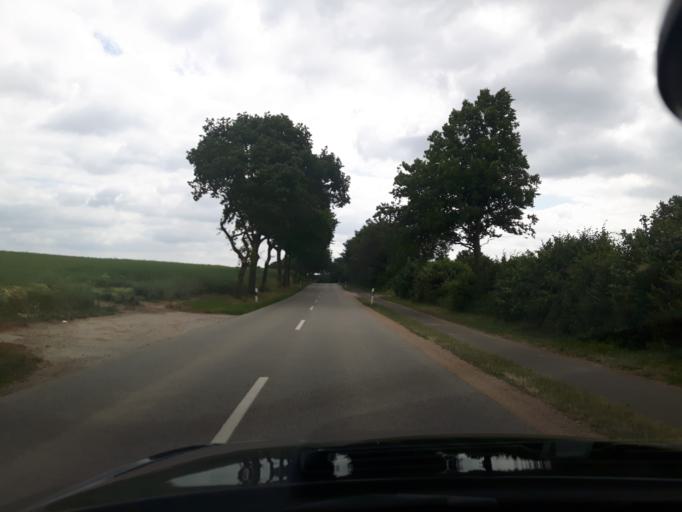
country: DE
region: Schleswig-Holstein
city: Neustadt in Holstein
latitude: 54.1019
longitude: 10.8446
